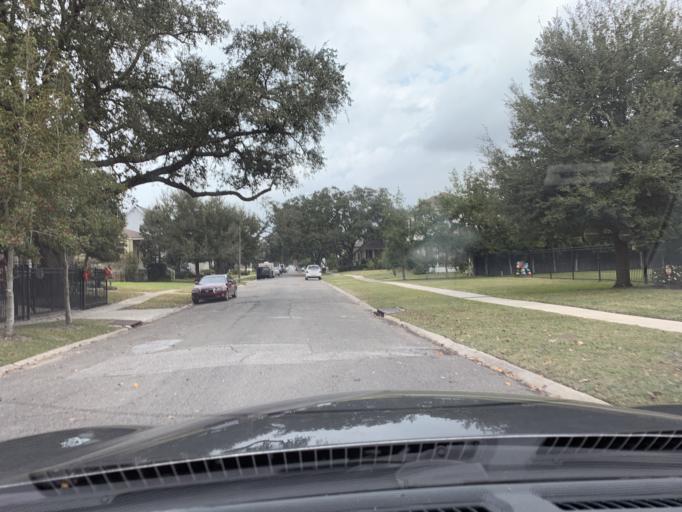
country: US
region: Louisiana
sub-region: Jefferson Parish
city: Metairie
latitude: 30.0138
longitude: -90.1027
